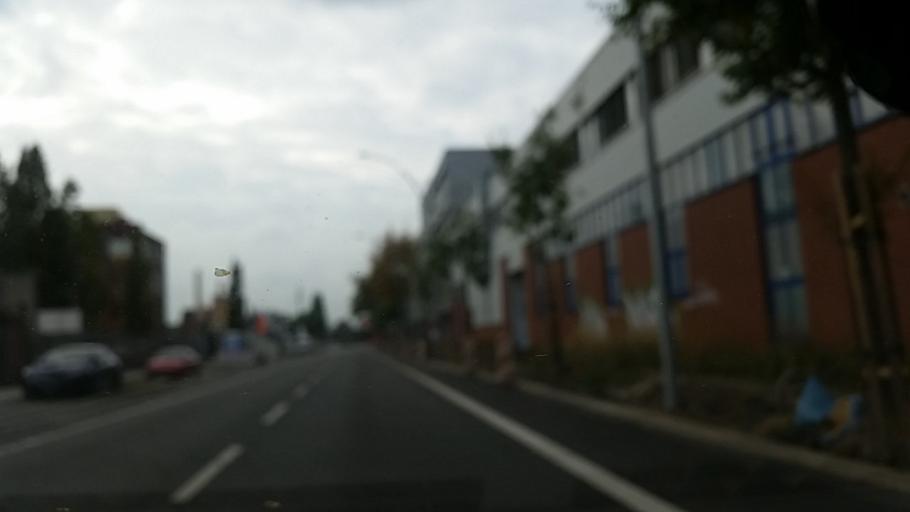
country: DE
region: Hamburg
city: Marienthal
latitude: 53.5344
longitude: 10.0859
